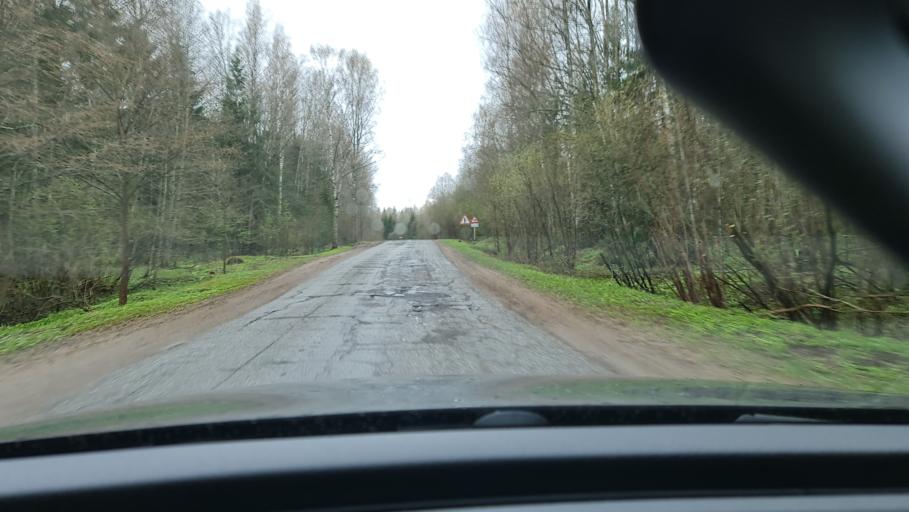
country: RU
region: Novgorod
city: Marevo
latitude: 57.2631
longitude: 32.0723
